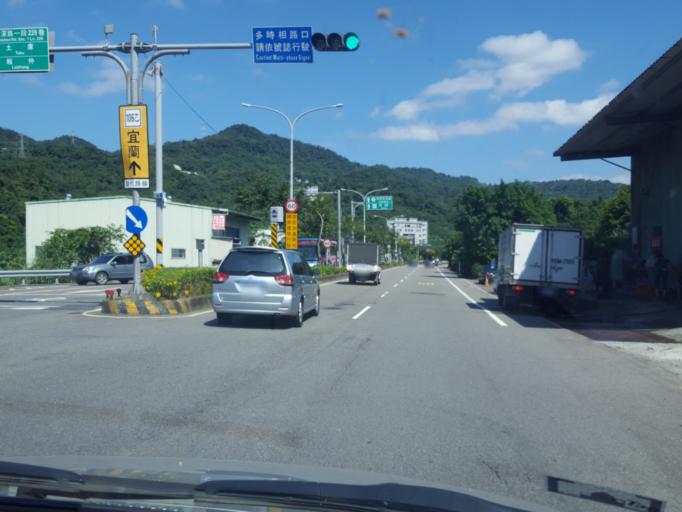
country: TW
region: Taipei
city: Taipei
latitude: 25.0057
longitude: 121.6312
